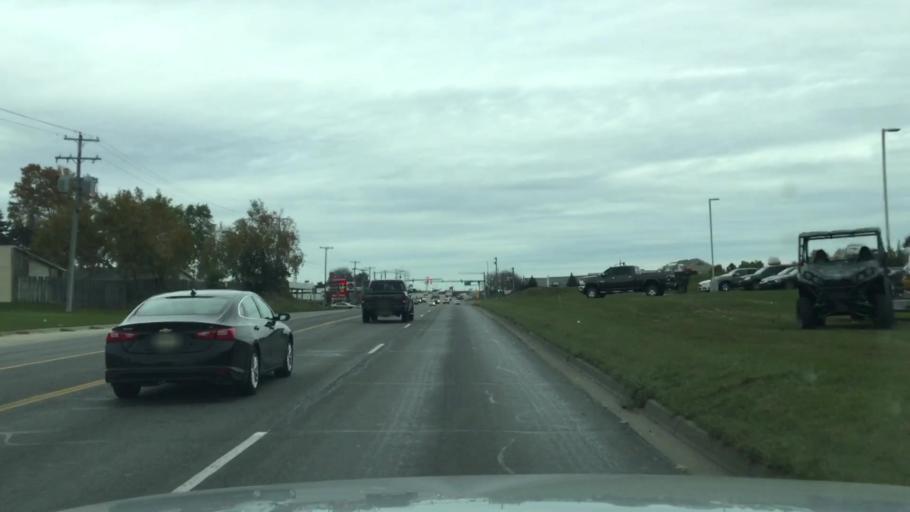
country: US
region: Michigan
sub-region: Kalamazoo County
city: Eastwood
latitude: 42.2523
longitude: -85.5308
